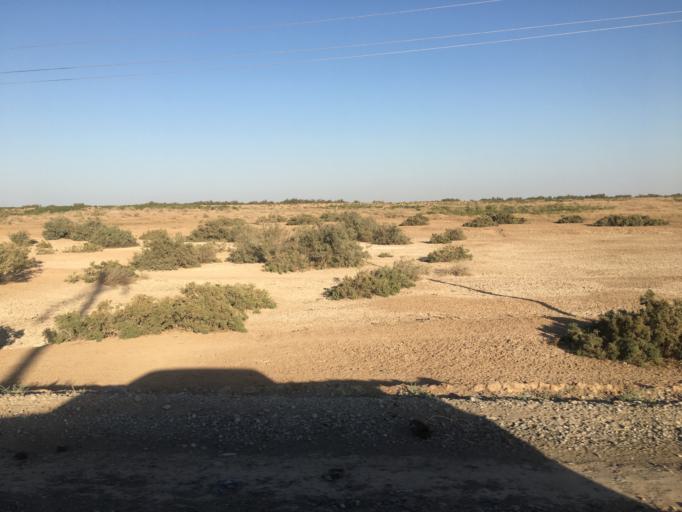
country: IR
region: Razavi Khorasan
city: Sarakhs
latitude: 37.1644
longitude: 61.2148
